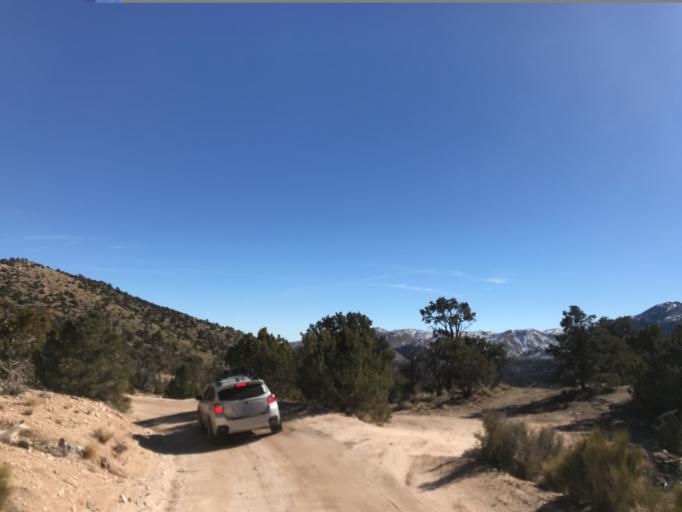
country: US
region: California
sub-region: San Bernardino County
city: Big Bear City
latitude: 34.2403
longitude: -116.6922
